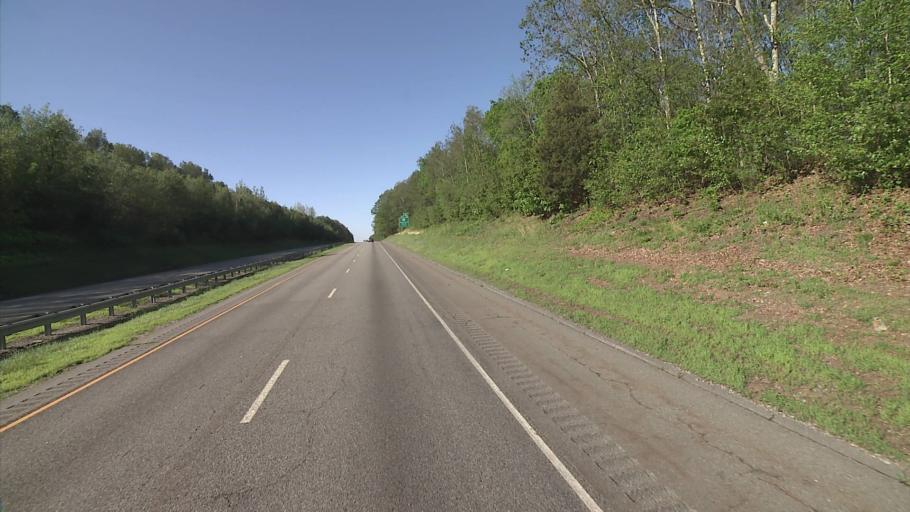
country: US
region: Connecticut
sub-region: Windham County
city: Moosup
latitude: 41.7030
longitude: -71.9009
